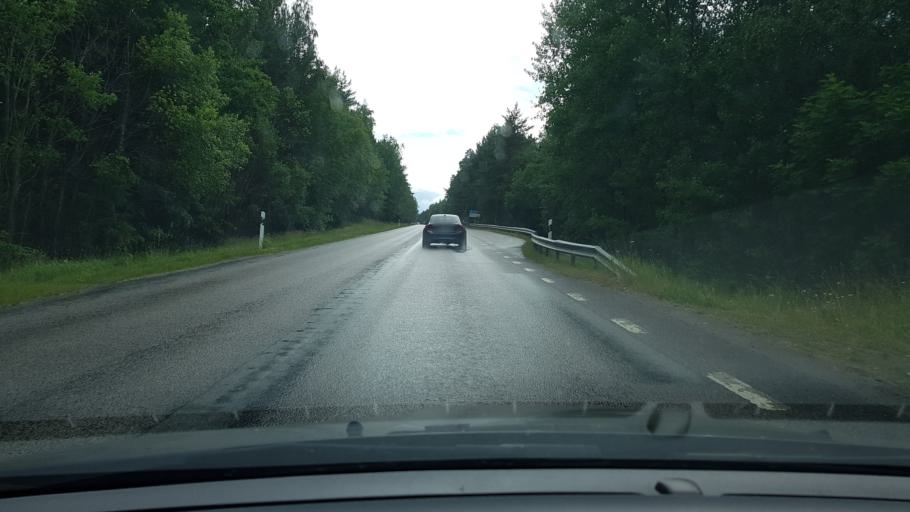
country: SE
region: Uppsala
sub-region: Uppsala Kommun
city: Saevja
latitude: 59.8112
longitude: 17.6915
